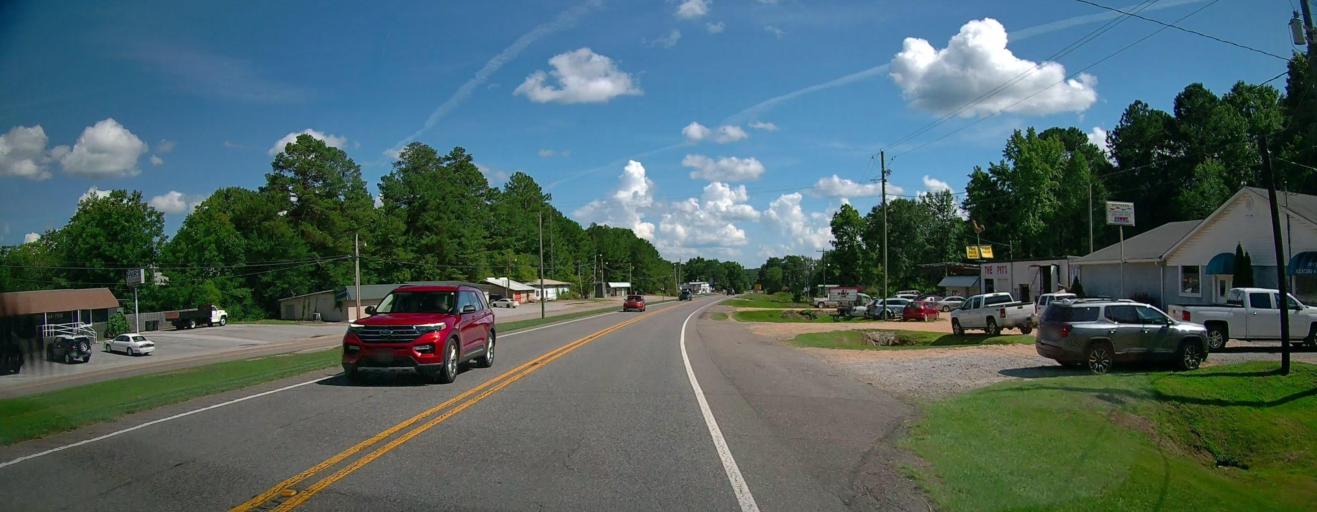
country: US
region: Alabama
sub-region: Pickens County
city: Gordo
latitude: 33.3286
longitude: -87.9118
